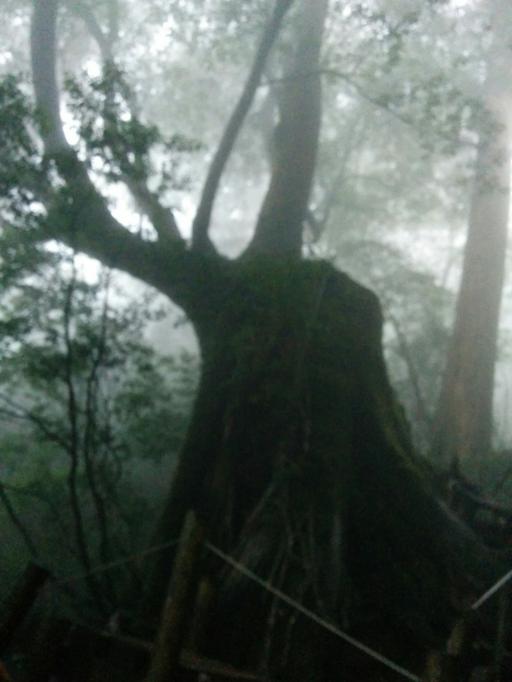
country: JP
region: Kagoshima
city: Nishinoomote
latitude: 30.3596
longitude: 130.5363
